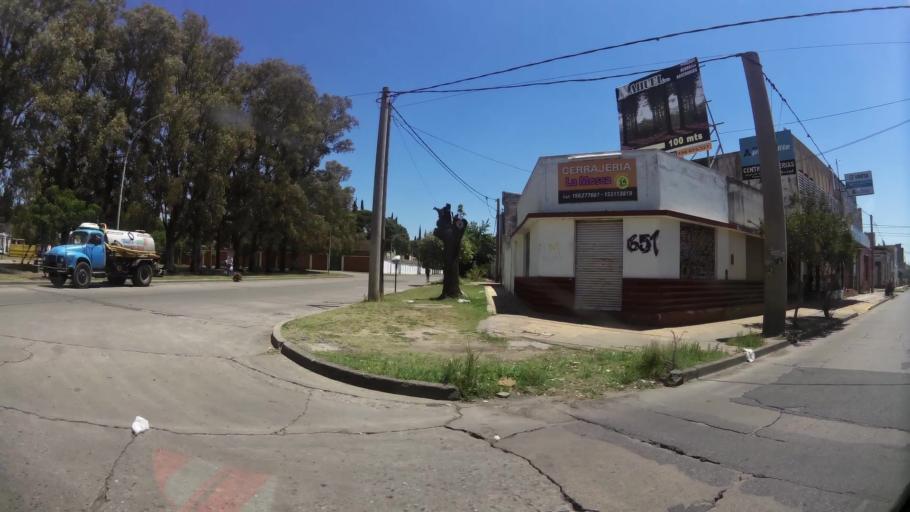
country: AR
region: Cordoba
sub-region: Departamento de Capital
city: Cordoba
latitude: -31.4003
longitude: -64.2107
